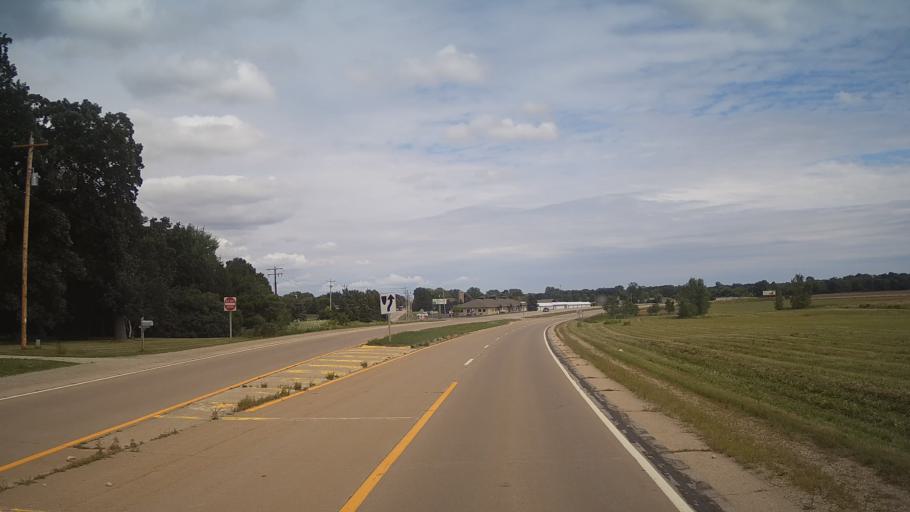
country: US
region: Wisconsin
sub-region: Winnebago County
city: Oshkosh
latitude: 44.0328
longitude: -88.6263
